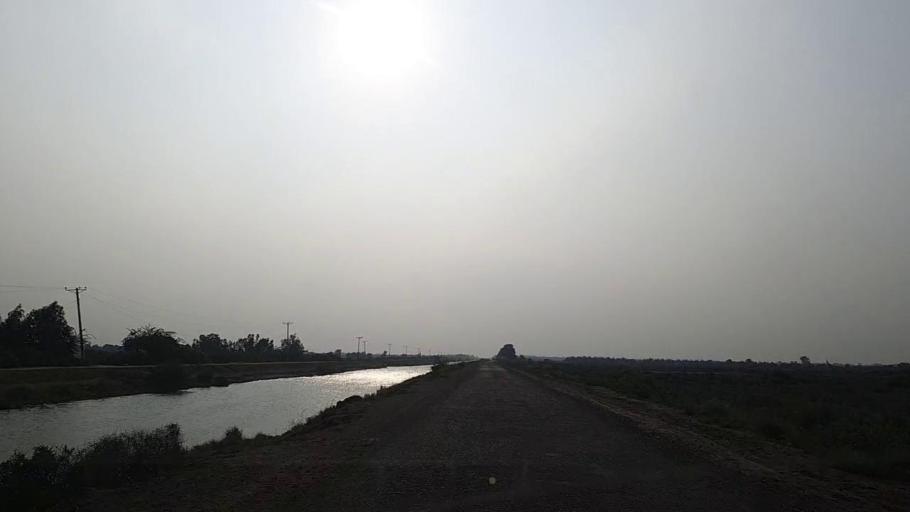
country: PK
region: Sindh
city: Mirpur Sakro
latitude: 24.6332
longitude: 67.5825
